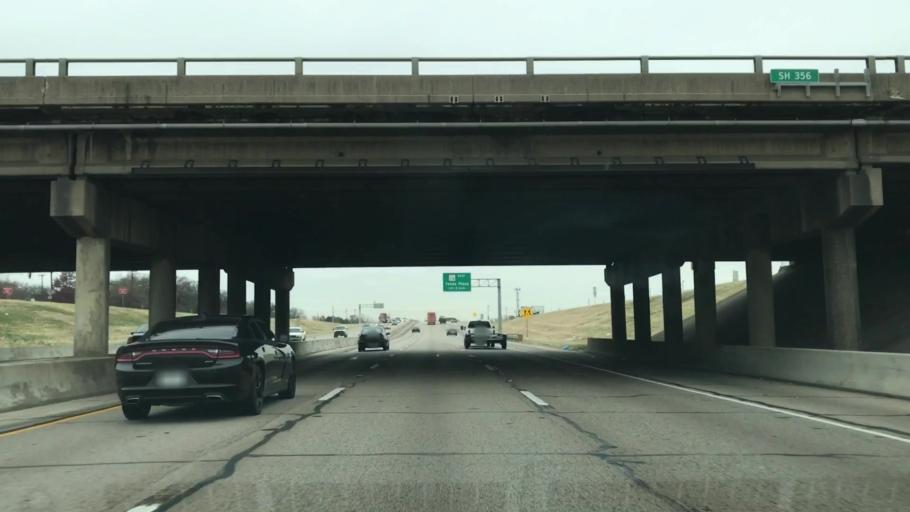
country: US
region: Texas
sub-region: Dallas County
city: Irving
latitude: 32.8094
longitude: -96.9215
